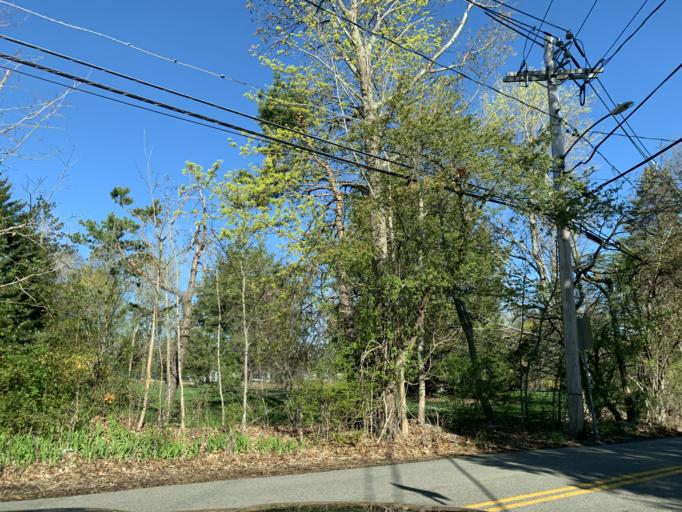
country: US
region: Massachusetts
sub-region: Norfolk County
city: Westwood
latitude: 42.2319
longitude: -71.2155
